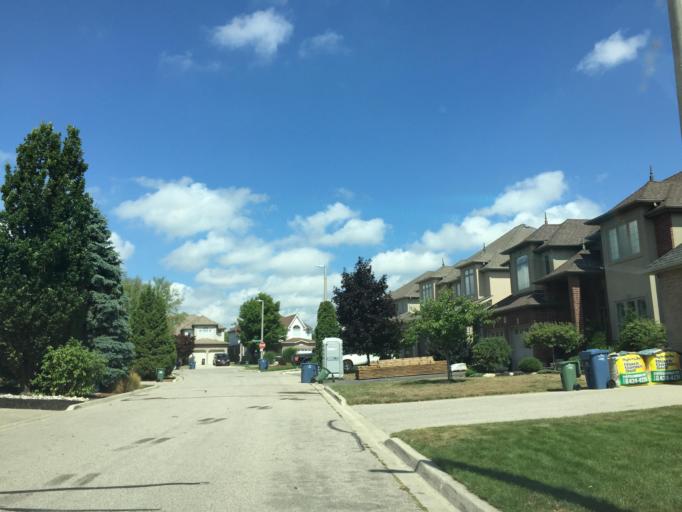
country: CA
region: Ontario
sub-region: Wellington County
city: Guelph
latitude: 43.5158
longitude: -80.1842
